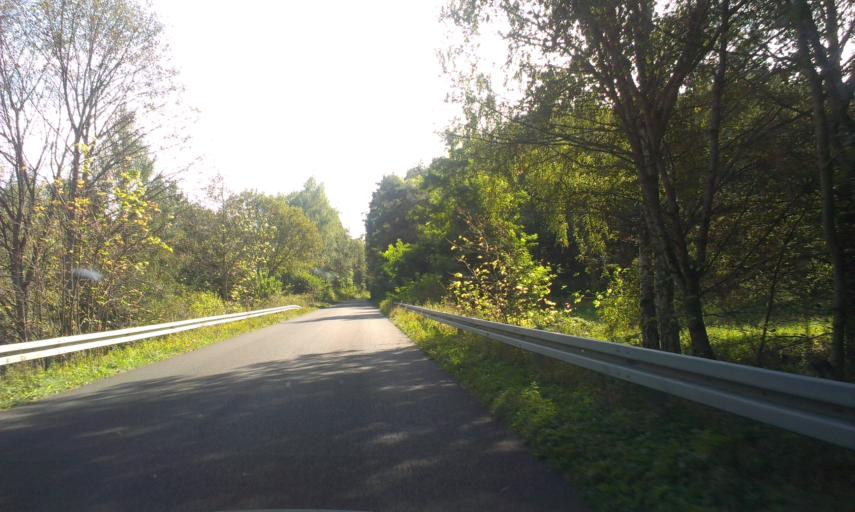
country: PL
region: Greater Poland Voivodeship
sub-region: Powiat zlotowski
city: Zlotow
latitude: 53.4900
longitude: 16.9880
